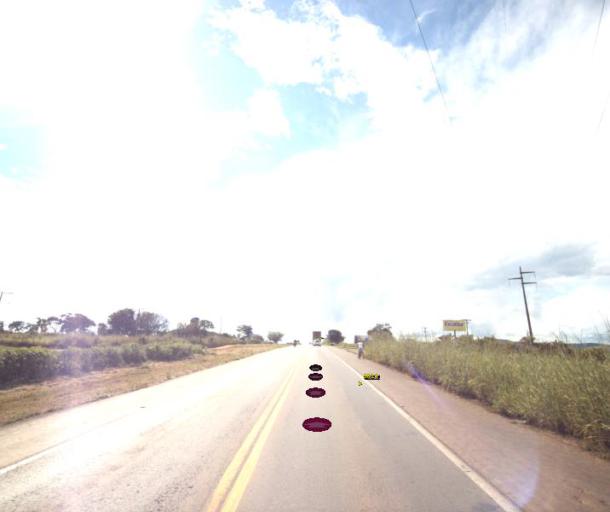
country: BR
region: Goias
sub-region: Jaragua
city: Jaragua
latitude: -15.7420
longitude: -49.3204
